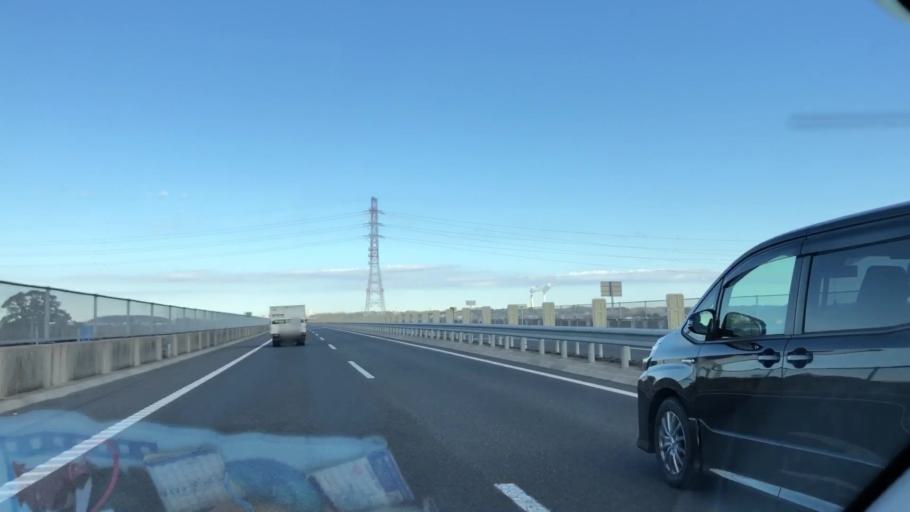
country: JP
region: Chiba
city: Kisarazu
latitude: 35.3966
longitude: 139.9678
